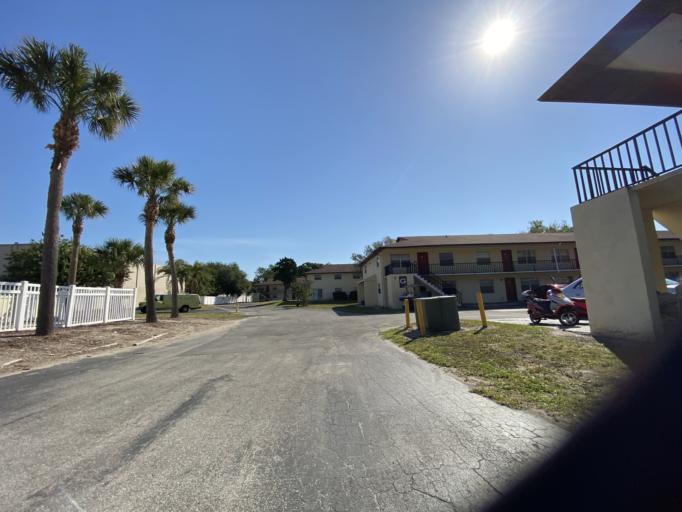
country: US
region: Florida
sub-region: Volusia County
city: South Daytona
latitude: 29.1716
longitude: -81.0047
